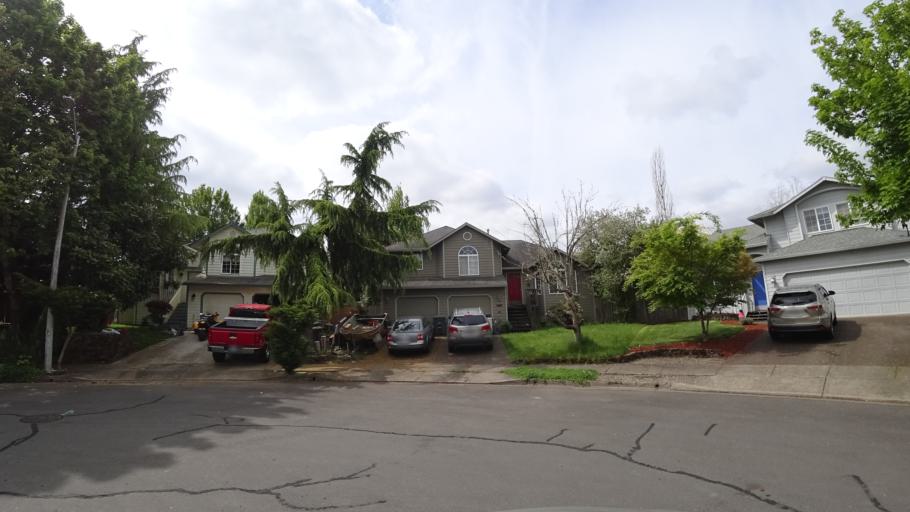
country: US
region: Oregon
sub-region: Washington County
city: Hillsboro
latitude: 45.5474
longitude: -122.9904
